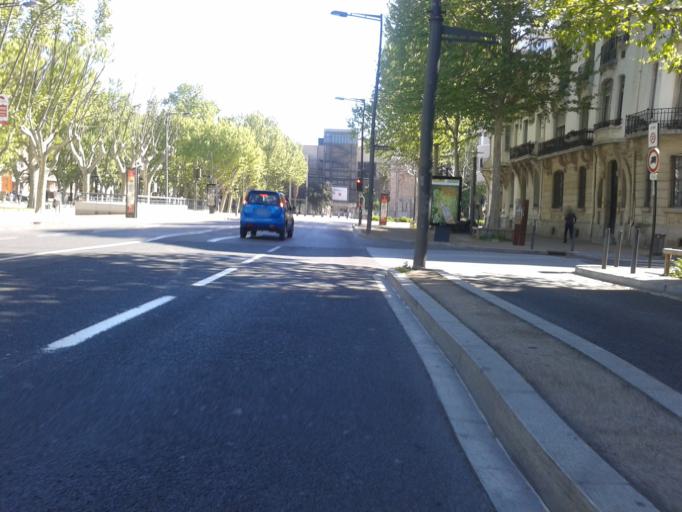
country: FR
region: Languedoc-Roussillon
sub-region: Departement des Pyrenees-Orientales
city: Perpignan
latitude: 42.7021
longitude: 2.8966
